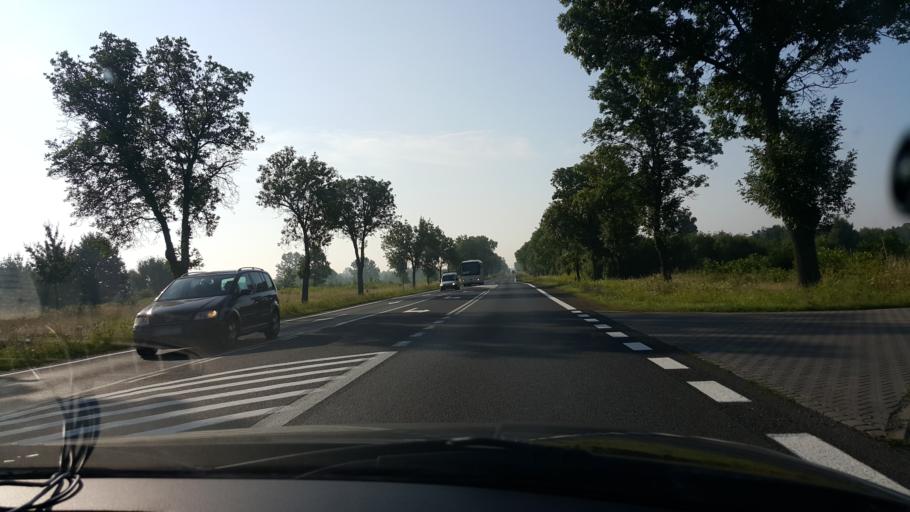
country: PL
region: Masovian Voivodeship
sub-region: Powiat radomski
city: Jedlnia-Letnisko
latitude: 51.4012
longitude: 21.2546
